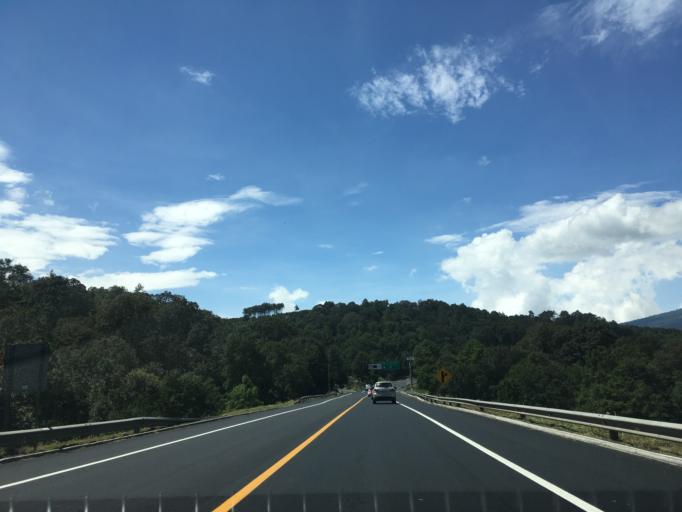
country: MX
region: Michoacan
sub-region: Patzcuaro
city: Santa Maria Huiramangaro (San Juan Tumbio)
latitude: 19.4841
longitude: -101.7253
